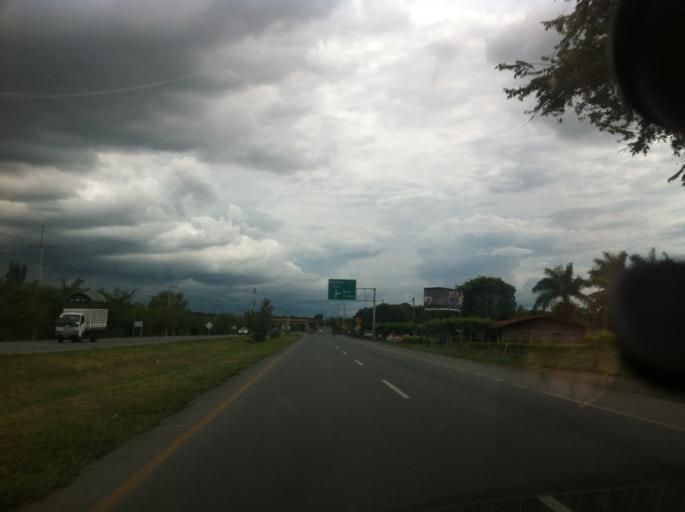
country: CO
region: Valle del Cauca
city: El Cerrito
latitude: 3.7051
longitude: -76.3198
